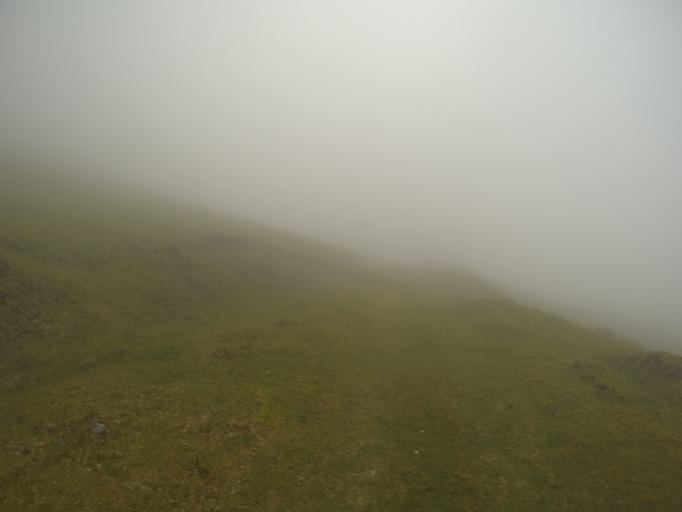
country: PT
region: Madeira
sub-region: Porto Moniz
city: Porto Moniz
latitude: 32.8123
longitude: -17.1435
